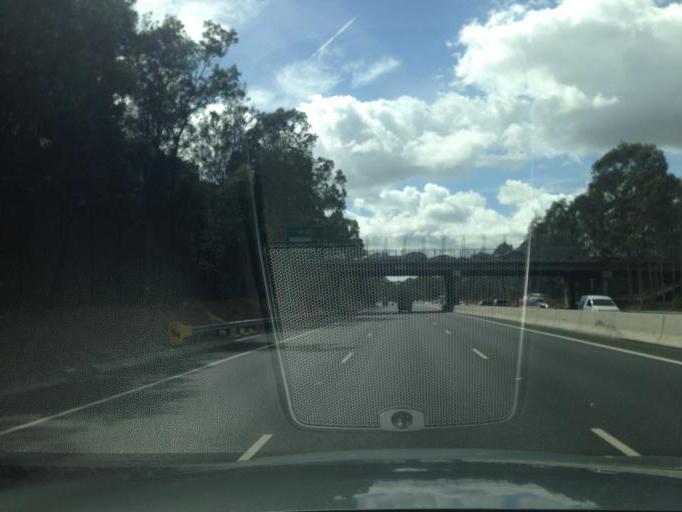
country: AU
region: New South Wales
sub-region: Bankstown
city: Milperra
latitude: -33.9435
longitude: 150.9925
